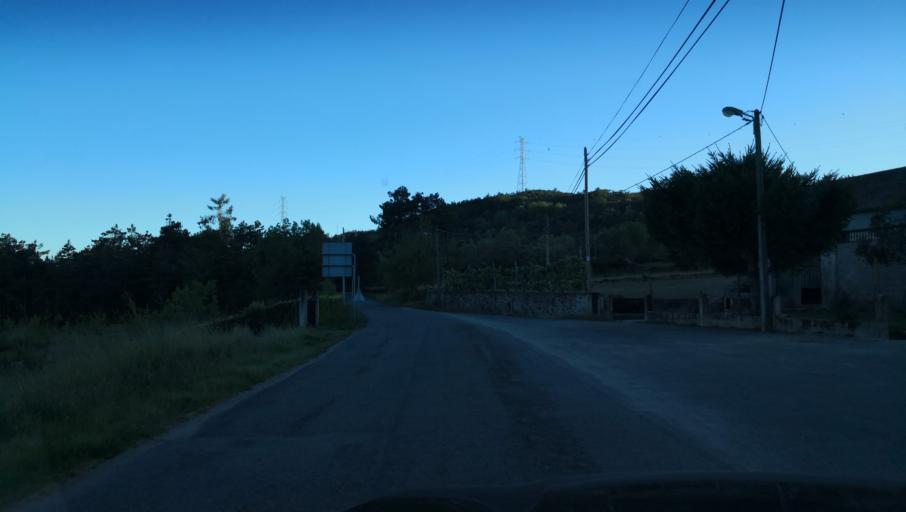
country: PT
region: Vila Real
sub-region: Sabrosa
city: Sabrosa
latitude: 41.3435
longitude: -7.6229
